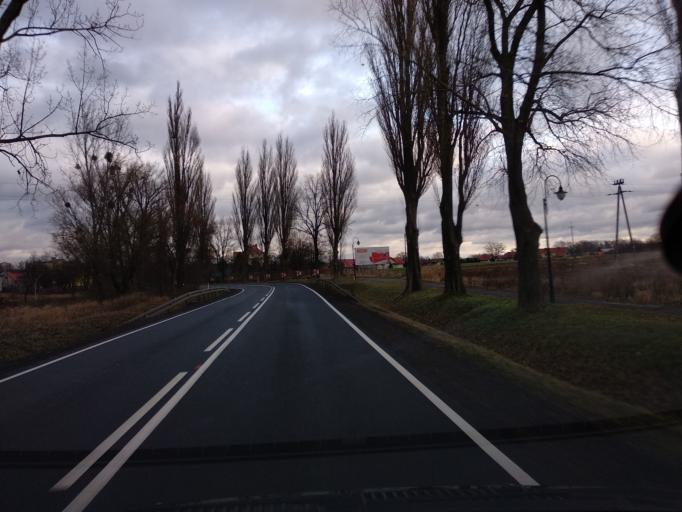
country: PL
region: Lower Silesian Voivodeship
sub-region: Powiat olesnicki
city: Miedzyborz
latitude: 51.3921
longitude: 17.6630
